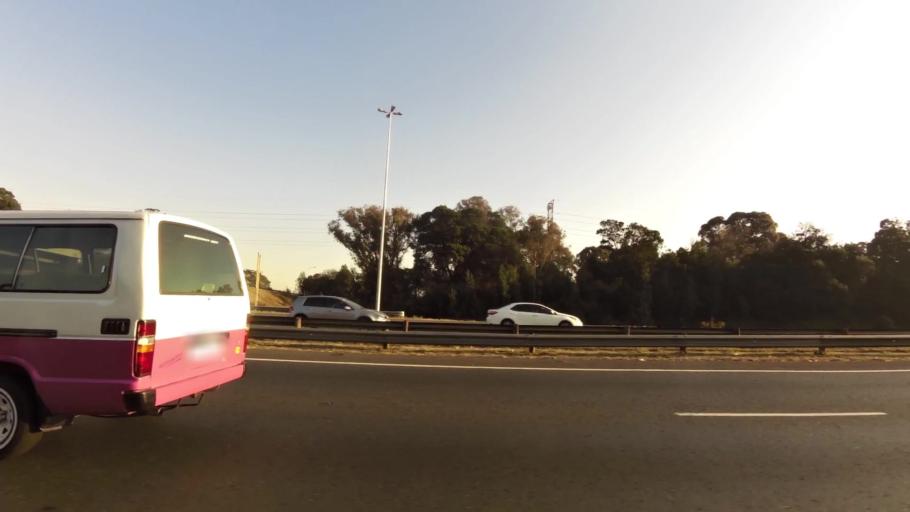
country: ZA
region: Gauteng
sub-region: City of Johannesburg Metropolitan Municipality
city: Johannesburg
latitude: -26.2521
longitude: 27.9955
